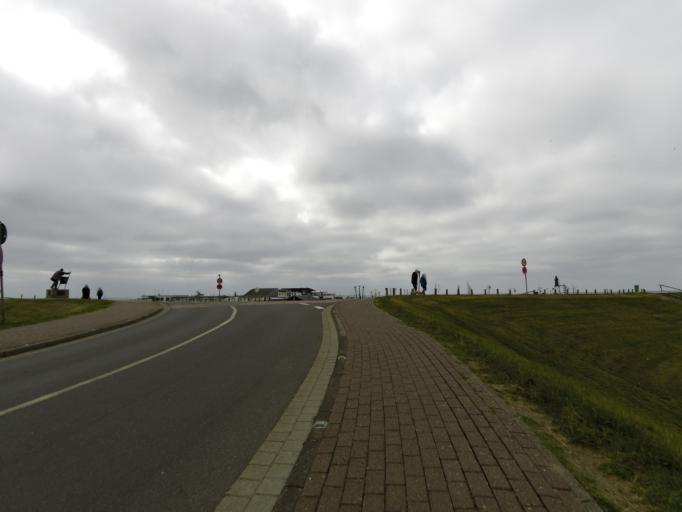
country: DE
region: Lower Saxony
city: Padingbuttel
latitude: 53.7373
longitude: 8.5184
